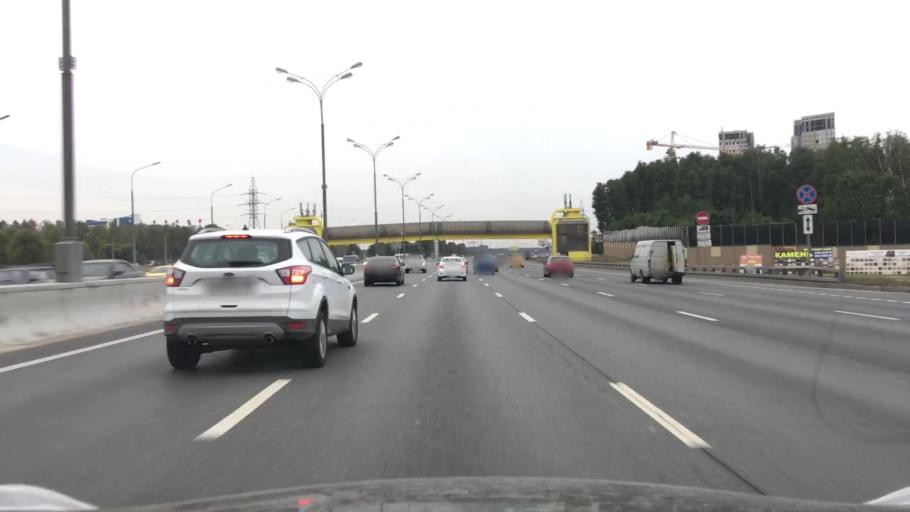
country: RU
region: Moscow
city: Strogino
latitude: 55.8036
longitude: 37.3863
